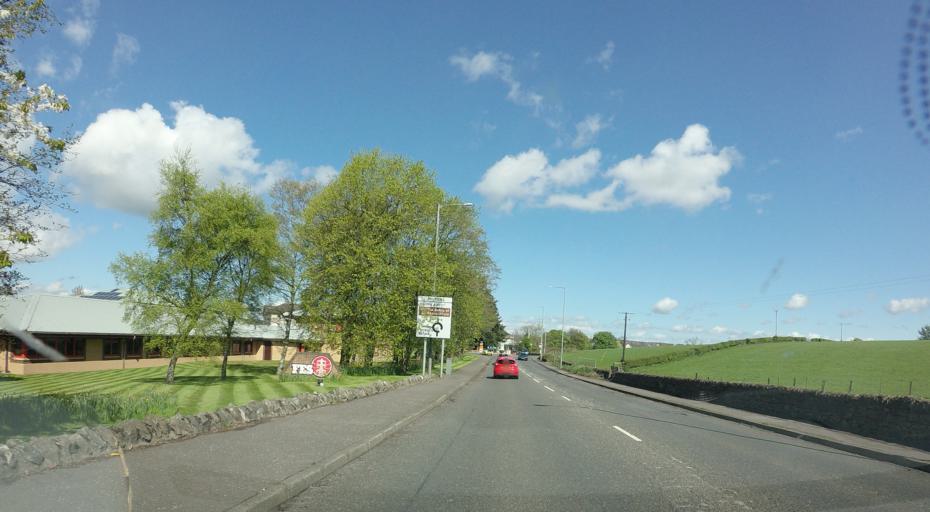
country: GB
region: Scotland
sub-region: Stirling
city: Bannockburn
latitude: 56.0833
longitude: -3.9258
